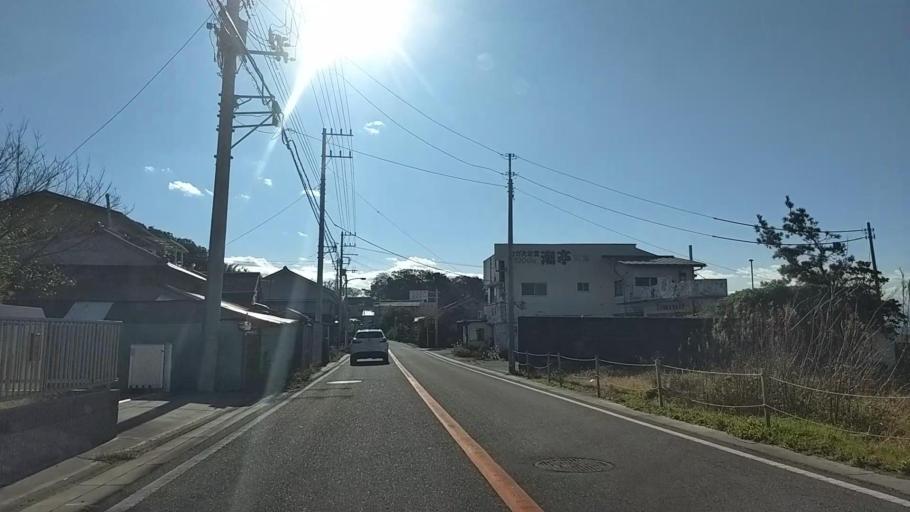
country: JP
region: Chiba
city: Futtsu
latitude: 35.1489
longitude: 139.8310
